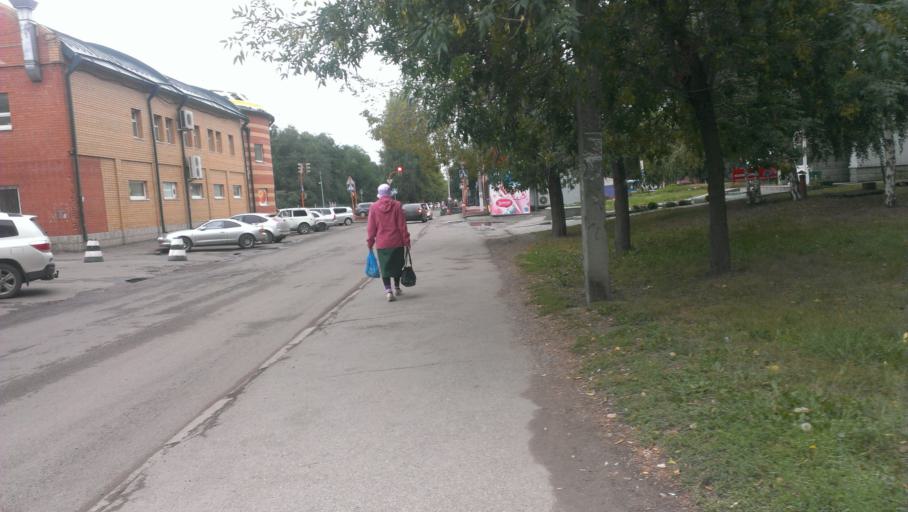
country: RU
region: Altai Krai
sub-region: Gorod Barnaulskiy
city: Barnaul
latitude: 53.3709
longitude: 83.6902
